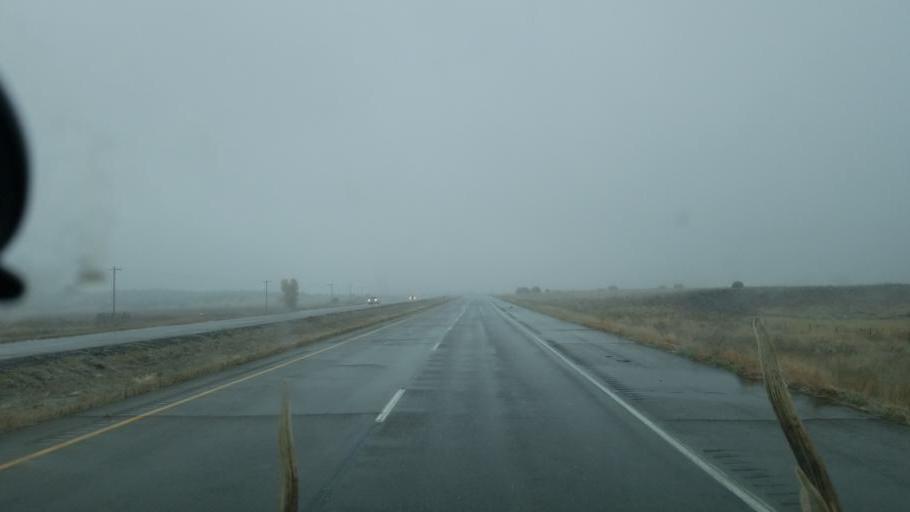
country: US
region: Colorado
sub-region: Pueblo County
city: Colorado City
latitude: 38.0247
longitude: -104.7351
